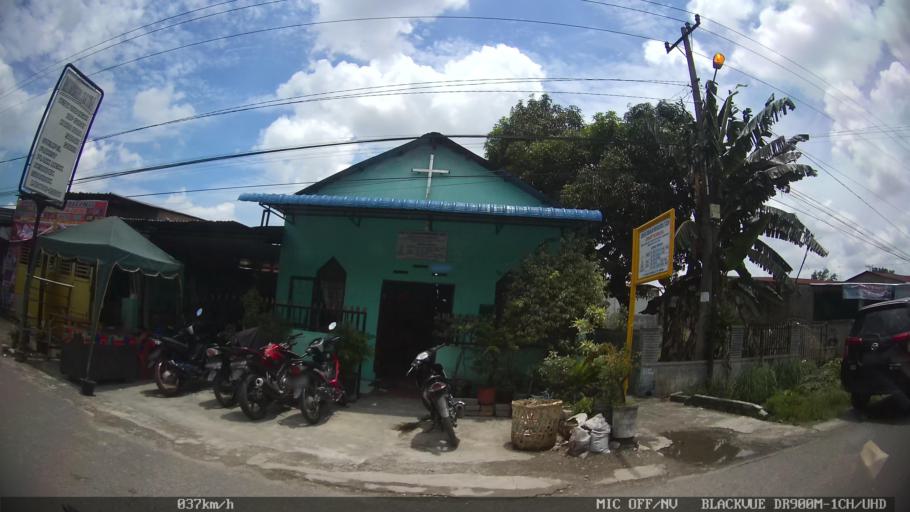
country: ID
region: North Sumatra
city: Medan
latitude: 3.6051
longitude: 98.7122
